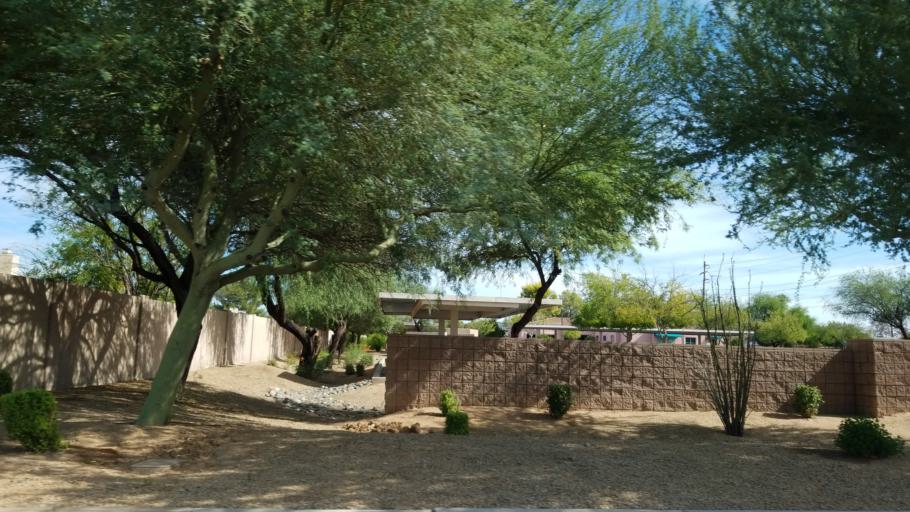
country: US
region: Arizona
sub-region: Maricopa County
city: Peoria
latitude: 33.6436
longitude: -112.1872
